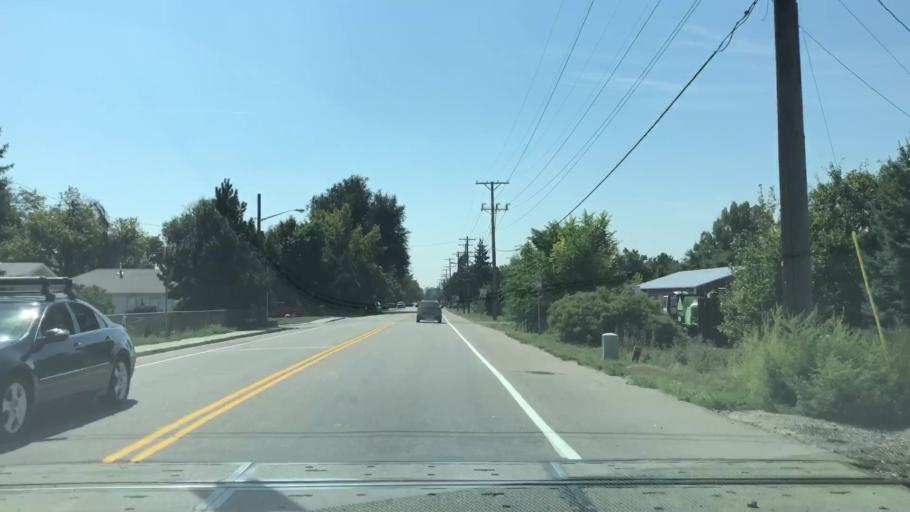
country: US
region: Colorado
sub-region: Larimer County
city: Loveland
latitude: 40.4002
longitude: -105.0589
